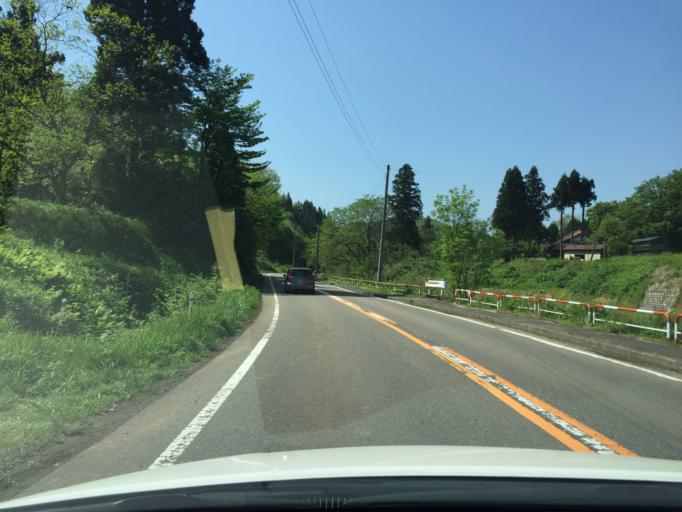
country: JP
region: Niigata
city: Muramatsu
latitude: 37.6404
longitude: 139.1120
